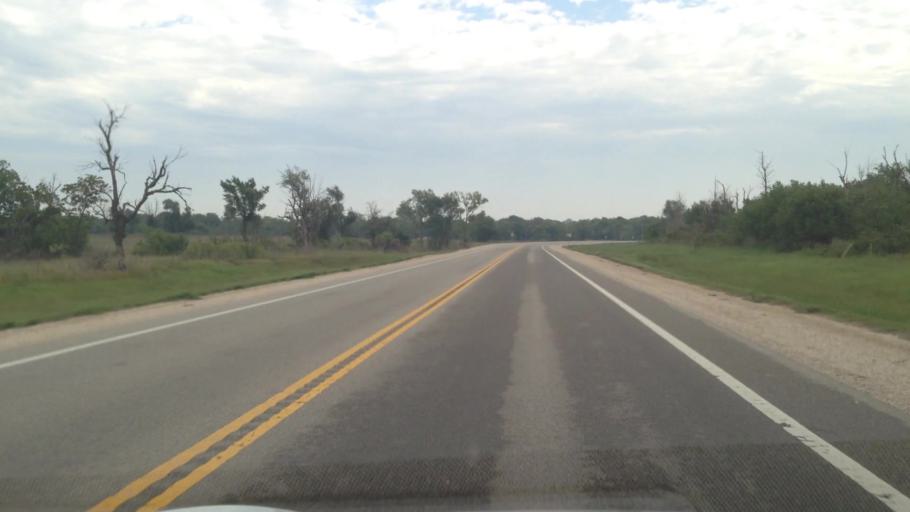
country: US
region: Kansas
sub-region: Allen County
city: Iola
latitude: 37.9083
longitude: -95.1043
